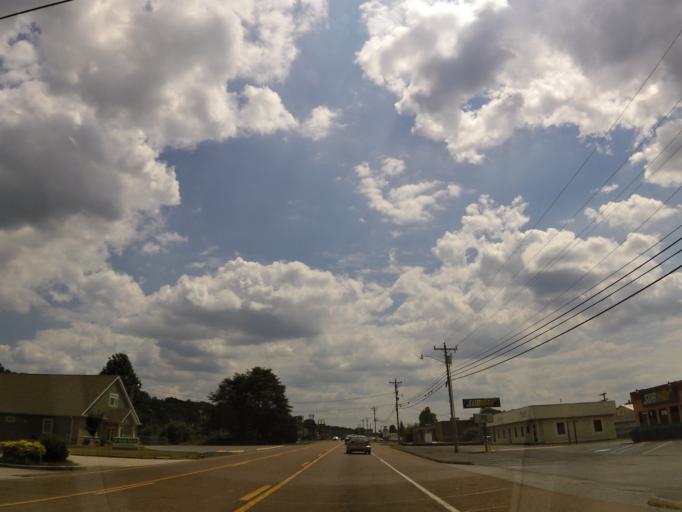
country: US
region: Tennessee
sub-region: Sequatchie County
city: Dunlap
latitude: 35.3657
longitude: -85.3933
